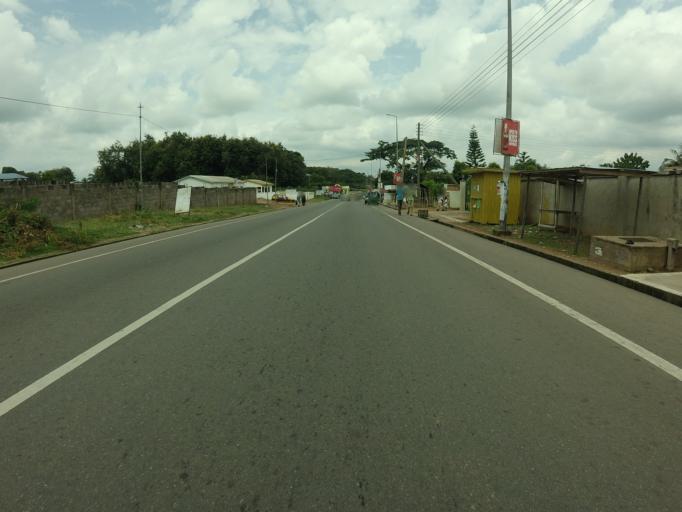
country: GH
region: Volta
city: Ho
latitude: 6.6004
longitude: 0.4719
